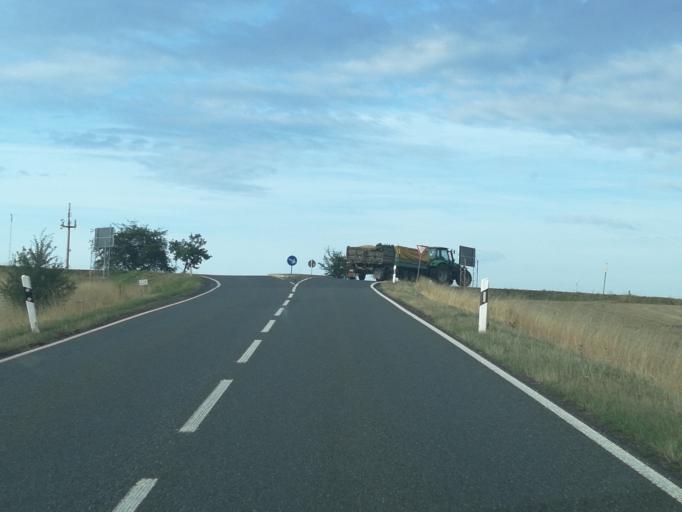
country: DE
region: Bavaria
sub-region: Upper Franconia
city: Regnitzlosau
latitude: 50.3091
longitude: 12.0291
